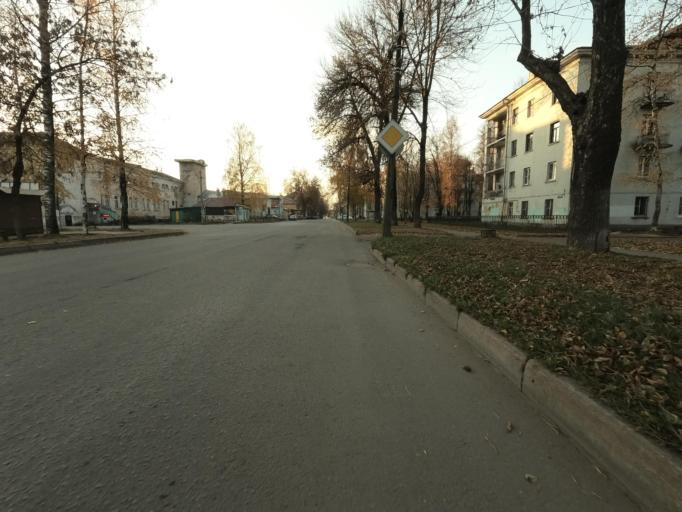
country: RU
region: Leningrad
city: Kirovsk
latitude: 59.8730
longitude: 30.9872
